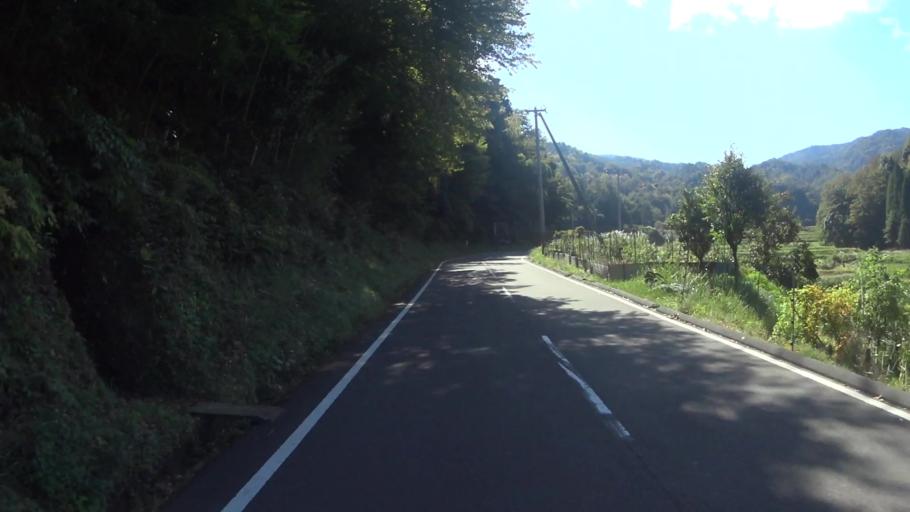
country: JP
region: Hyogo
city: Toyooka
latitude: 35.5372
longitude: 134.9376
